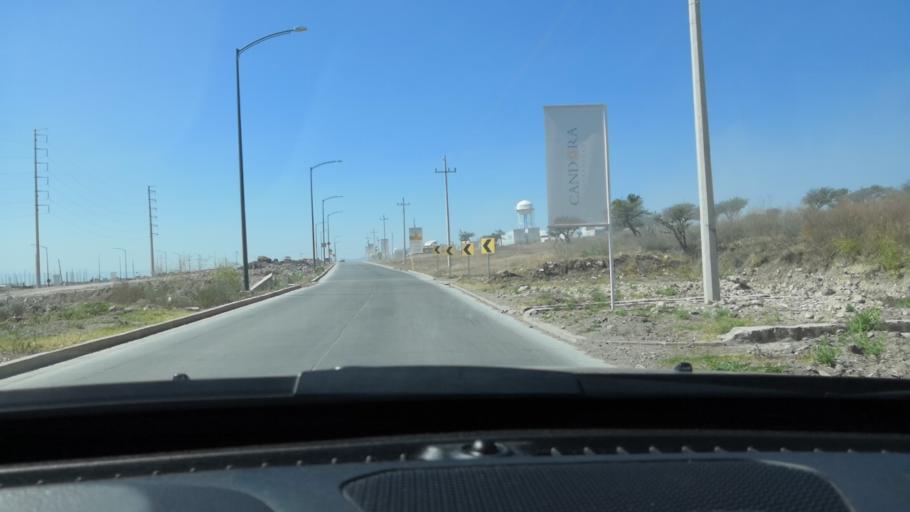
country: MX
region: Guanajuato
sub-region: Leon
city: Centro Familiar la Soledad
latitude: 21.1124
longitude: -101.7554
